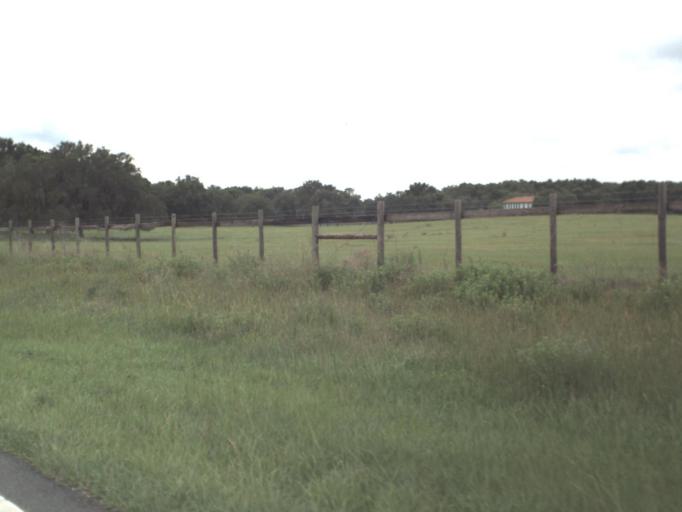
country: US
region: Florida
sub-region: Levy County
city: Williston Highlands
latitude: 29.2142
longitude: -82.4399
